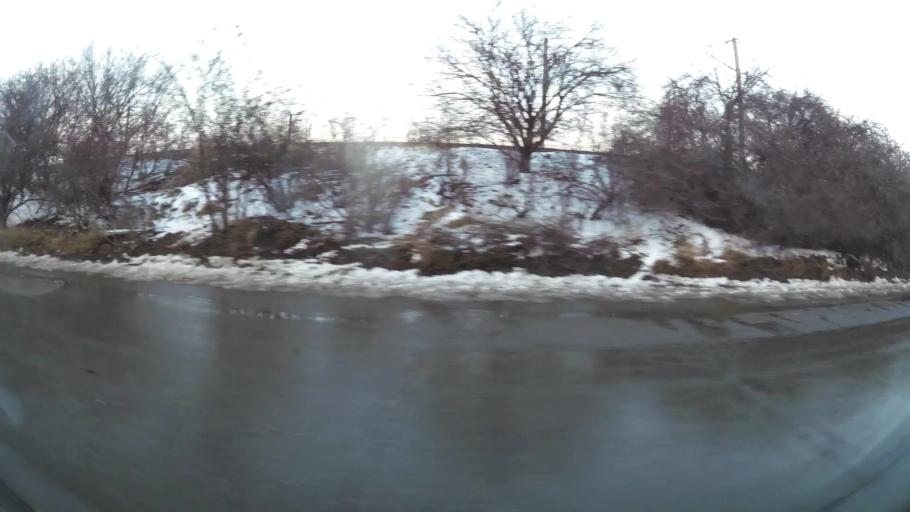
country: BG
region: Sofia-Capital
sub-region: Stolichna Obshtina
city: Sofia
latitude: 42.6891
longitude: 23.3739
